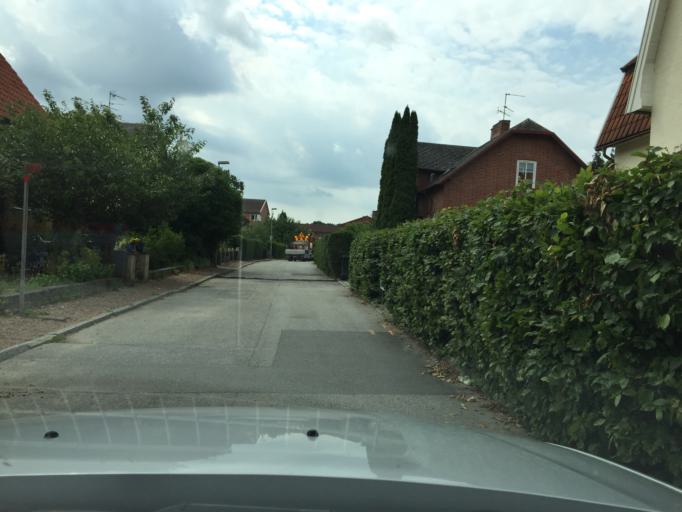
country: SE
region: Skane
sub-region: Lunds Kommun
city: Lund
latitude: 55.7042
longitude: 13.1644
